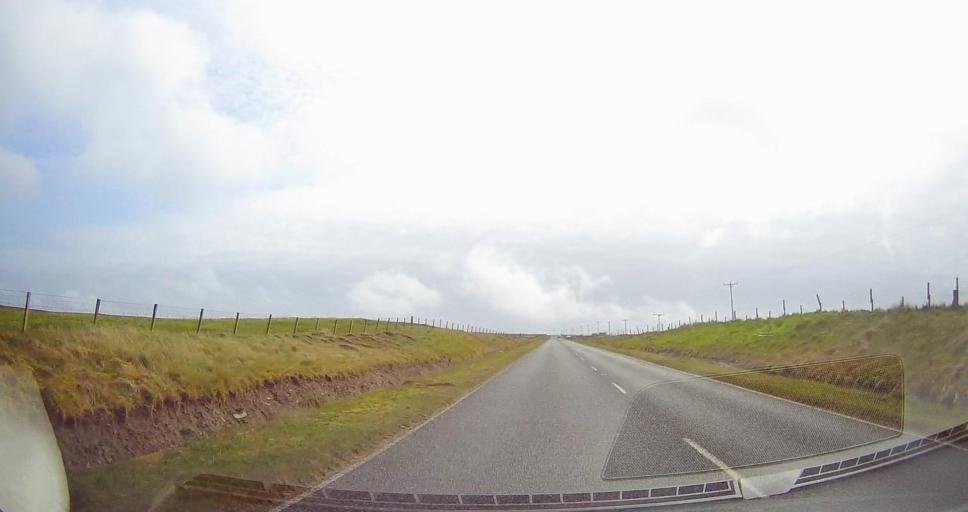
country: GB
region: Scotland
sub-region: Shetland Islands
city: Sandwick
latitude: 59.9049
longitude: -1.3025
